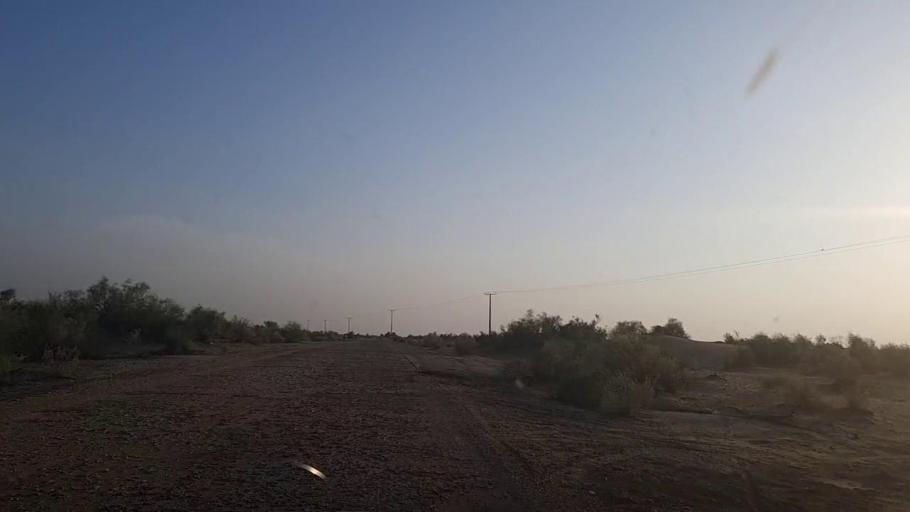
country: PK
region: Sindh
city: Khanpur
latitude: 27.6433
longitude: 69.4571
